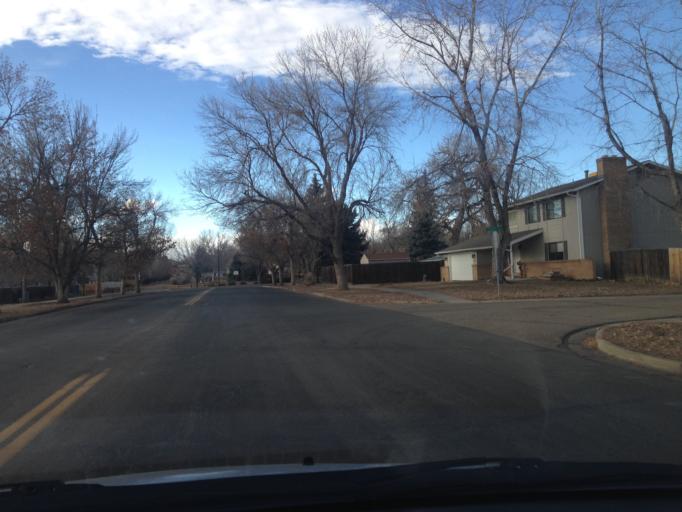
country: US
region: Colorado
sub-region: Boulder County
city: Lafayette
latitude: 39.9887
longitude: -105.1086
